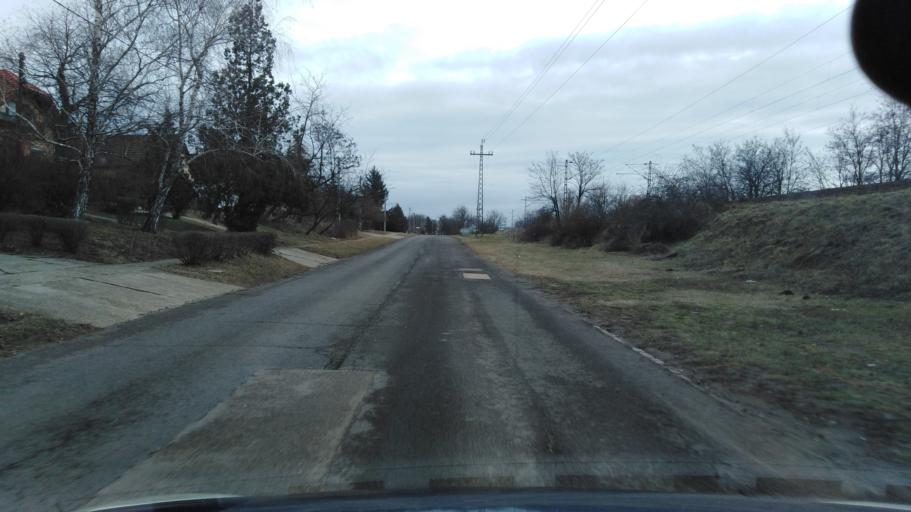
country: HU
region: Heves
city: Hatvan
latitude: 47.6745
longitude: 19.6968
